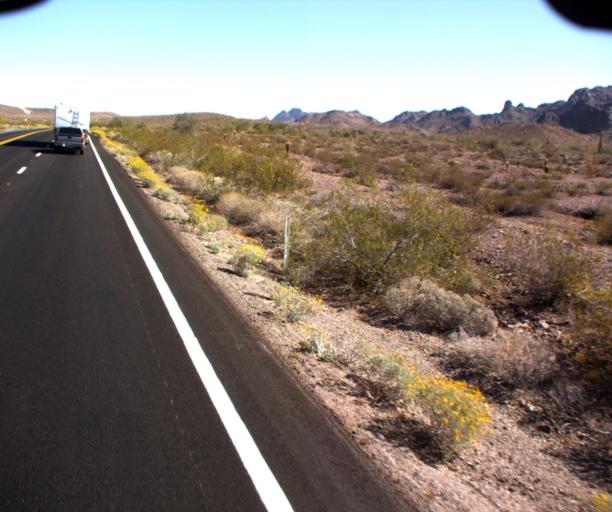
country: US
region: Arizona
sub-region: La Paz County
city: Quartzsite
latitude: 33.2199
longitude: -114.2590
